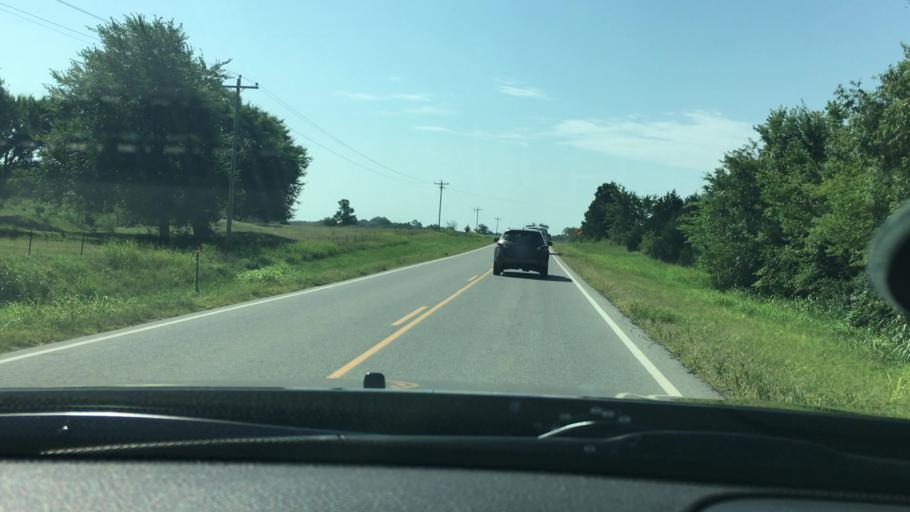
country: US
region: Oklahoma
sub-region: Coal County
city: Coalgate
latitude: 34.5818
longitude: -96.4112
